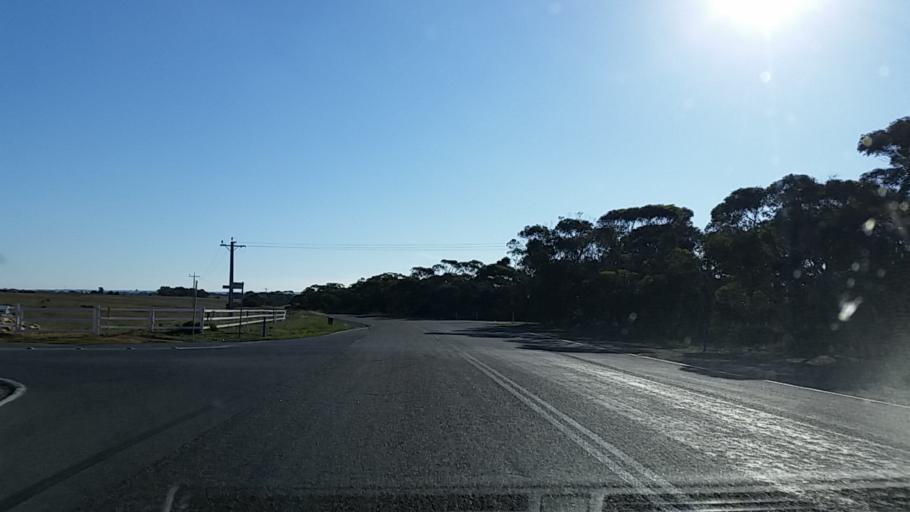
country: AU
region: South Australia
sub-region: Murray Bridge
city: Murray Bridge
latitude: -35.1241
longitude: 139.1831
